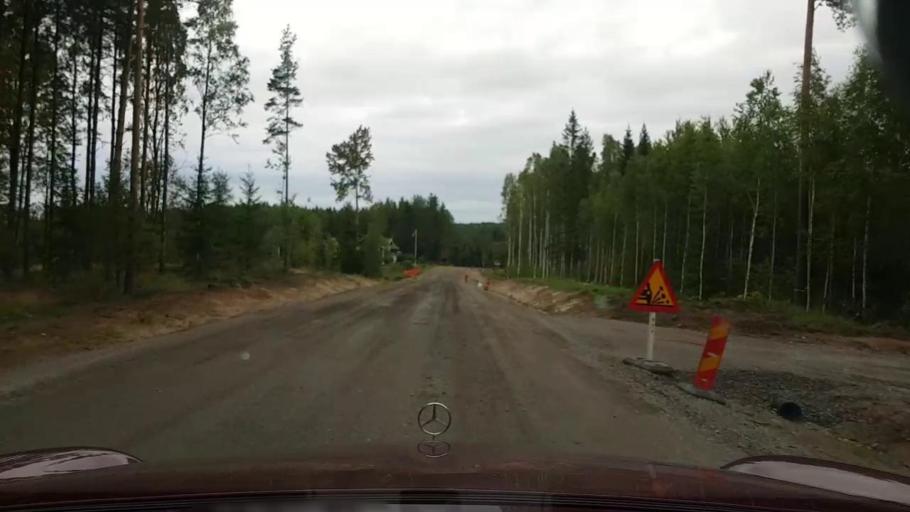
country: SE
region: Vaestra Goetaland
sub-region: Karlsborgs Kommun
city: Karlsborg
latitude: 58.7096
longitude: 14.5047
